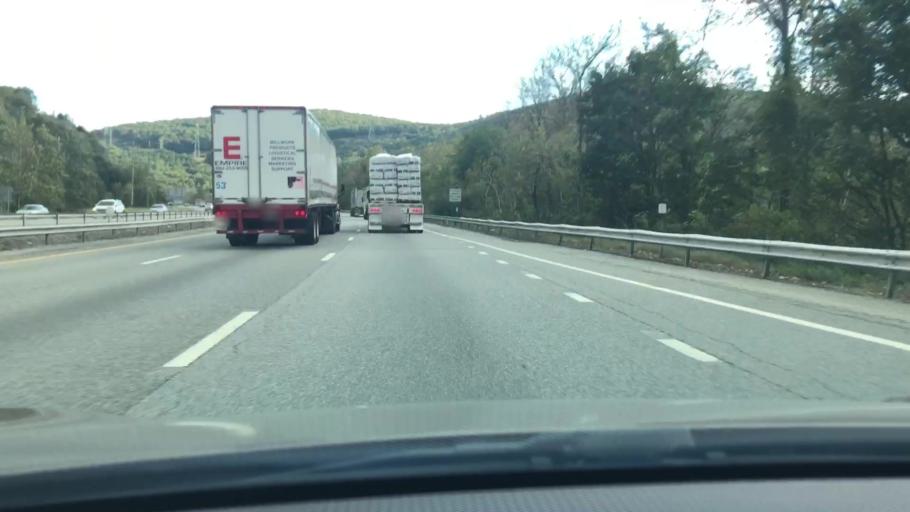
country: US
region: New York
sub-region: Rockland County
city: Sloatsburg
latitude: 41.1483
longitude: -74.1884
